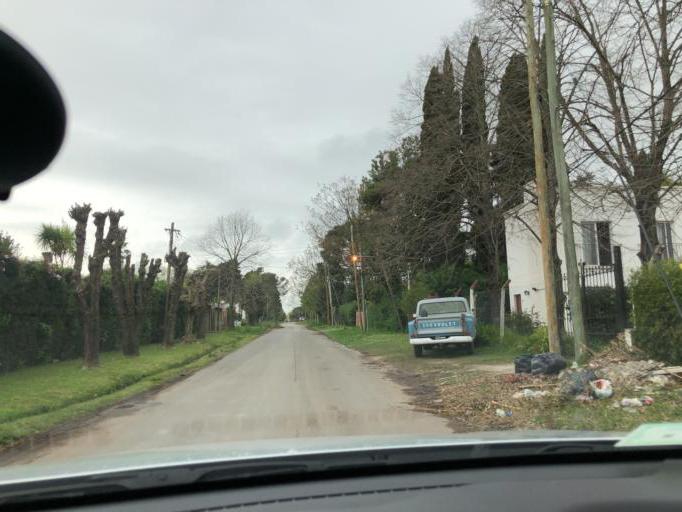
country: AR
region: Buenos Aires
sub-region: Partido de La Plata
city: La Plata
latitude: -34.8903
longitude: -58.0634
